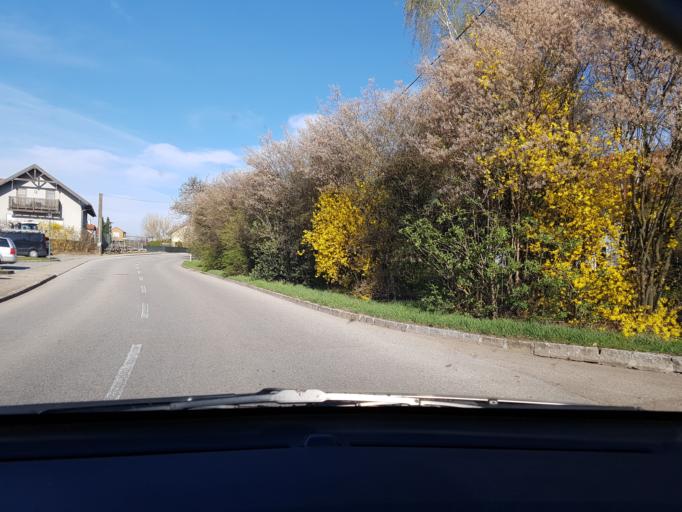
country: AT
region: Upper Austria
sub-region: Politischer Bezirk Linz-Land
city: Sankt Florian
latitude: 48.1429
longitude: 14.3780
